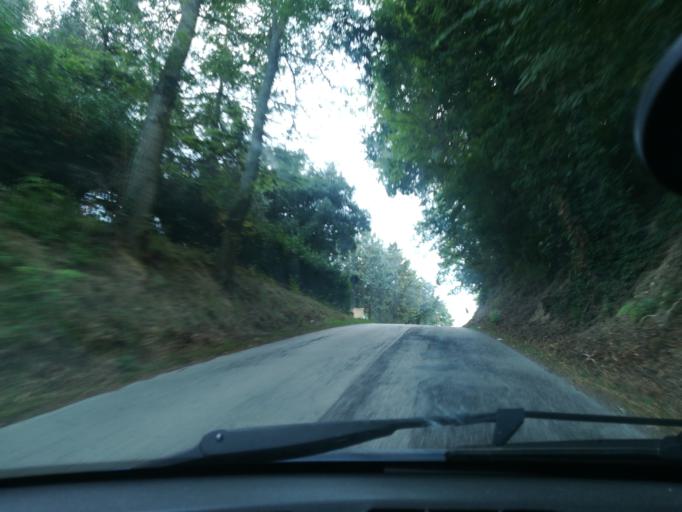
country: IT
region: The Marches
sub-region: Provincia di Macerata
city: Macerata
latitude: 43.3035
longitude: 13.4787
